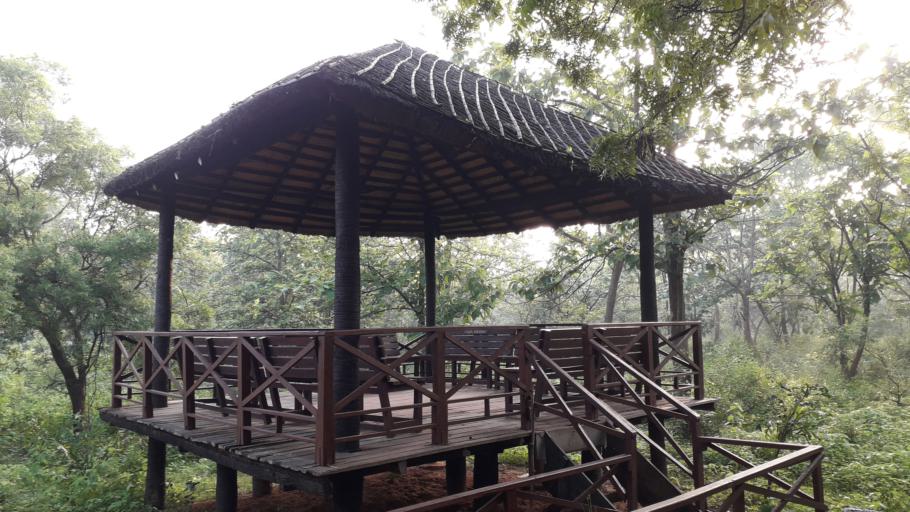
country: IN
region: Andhra Pradesh
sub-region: East Godavari
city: Rajahmundry
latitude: 17.0372
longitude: 81.8202
